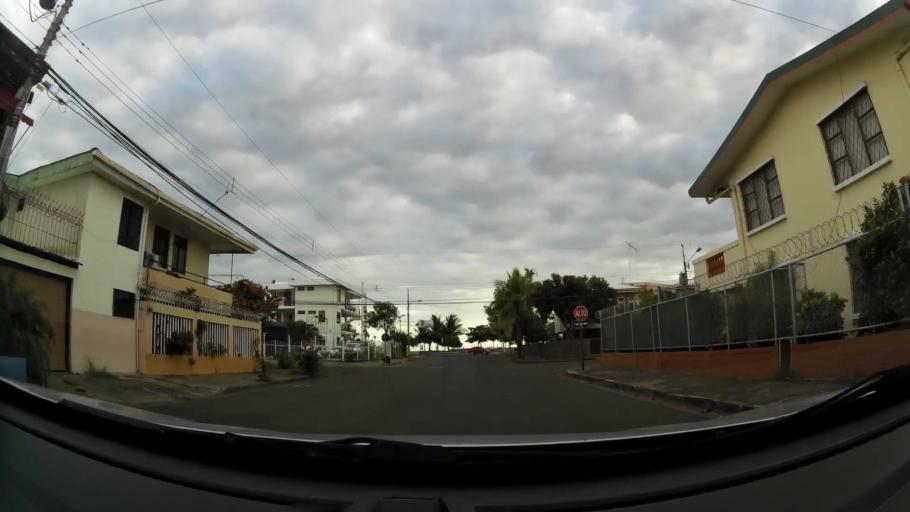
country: CR
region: Puntarenas
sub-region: Canton Central de Puntarenas
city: Puntarenas
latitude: 9.9754
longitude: -84.8478
